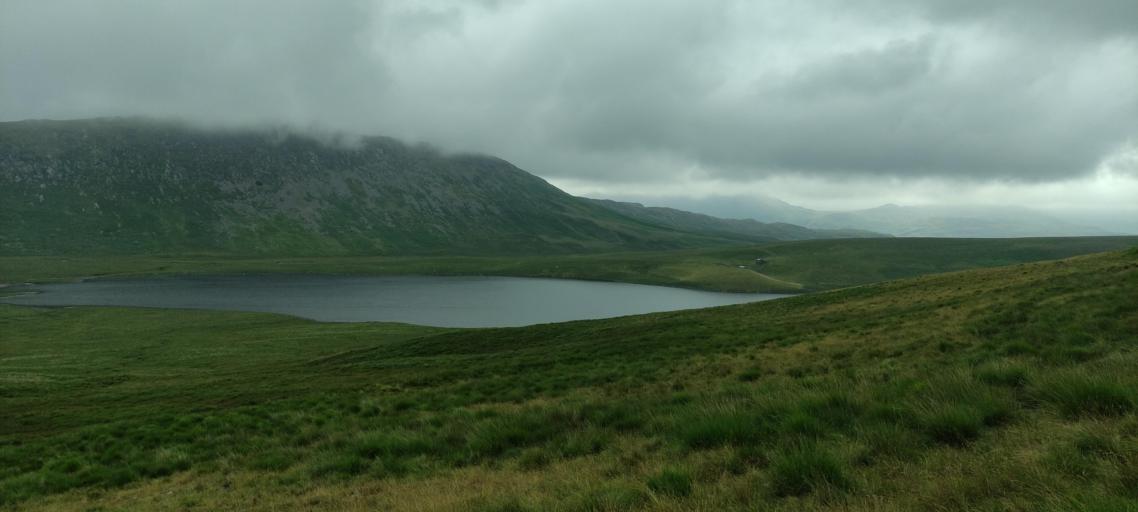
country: GB
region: England
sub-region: Cumbria
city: Seascale
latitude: 54.4322
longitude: -3.2687
